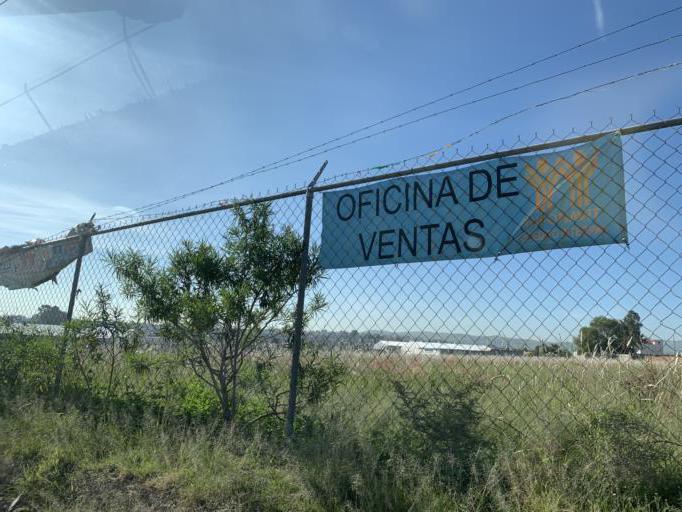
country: MX
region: Puebla
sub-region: Puebla
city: El Capulo (La Quebradora)
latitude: 18.9611
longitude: -98.2528
